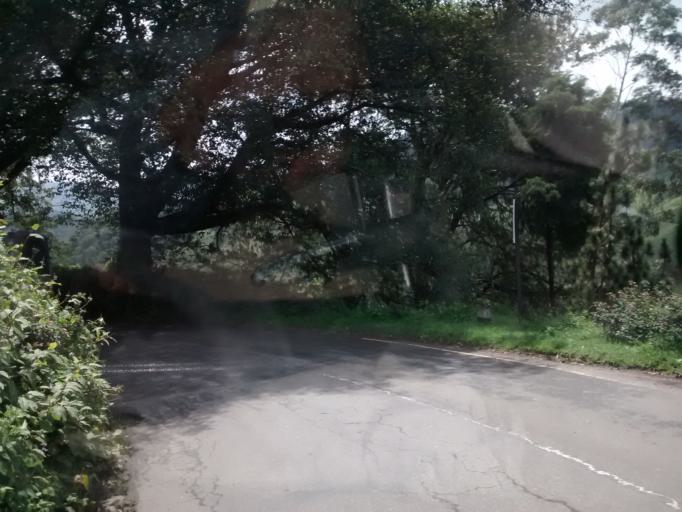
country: IN
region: Kerala
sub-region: Idukki
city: Munnar
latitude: 10.1044
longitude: 77.1197
